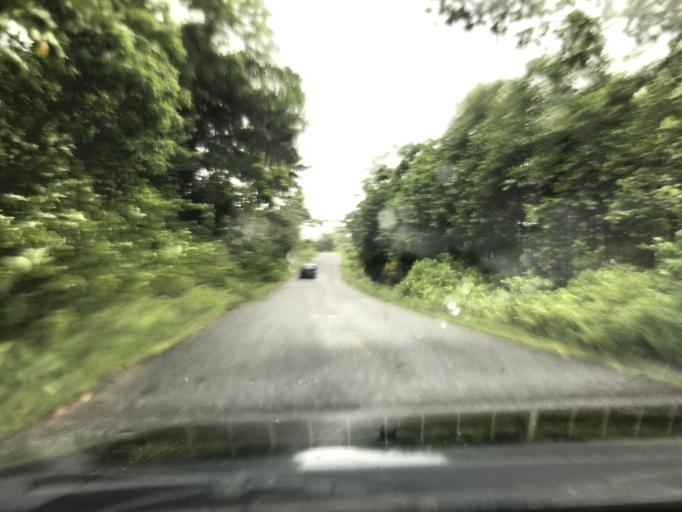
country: SB
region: Western Province
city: Gizo
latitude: -8.3231
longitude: 157.2570
